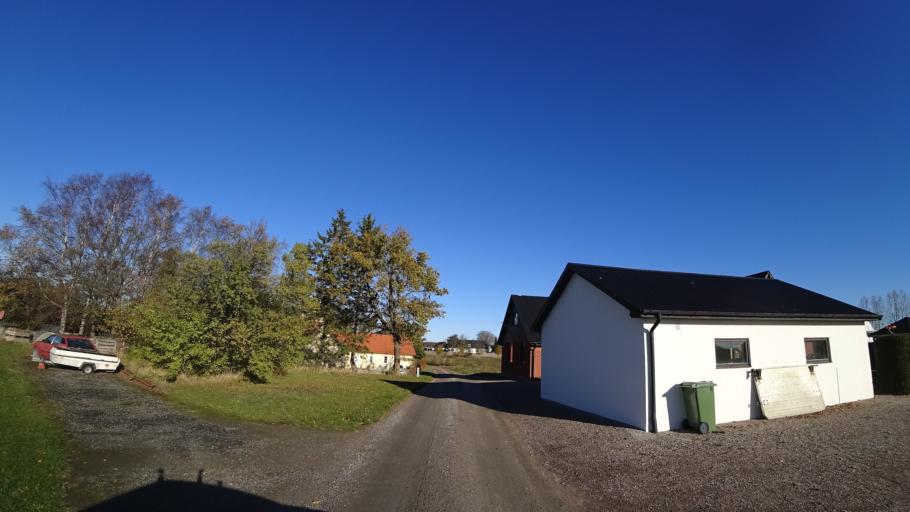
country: SE
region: Skane
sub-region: Svedala Kommun
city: Klagerup
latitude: 55.6494
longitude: 13.2898
